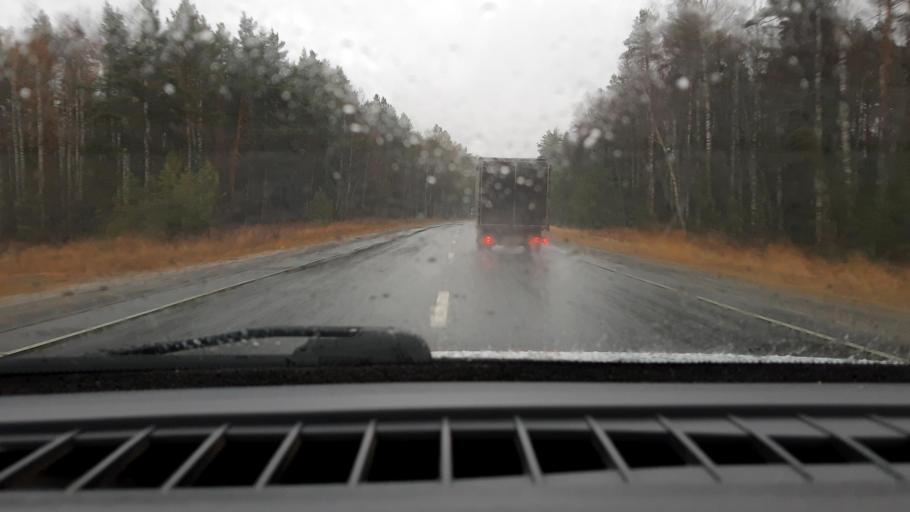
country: RU
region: Nizjnij Novgorod
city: Linda
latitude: 56.6636
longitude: 44.1312
